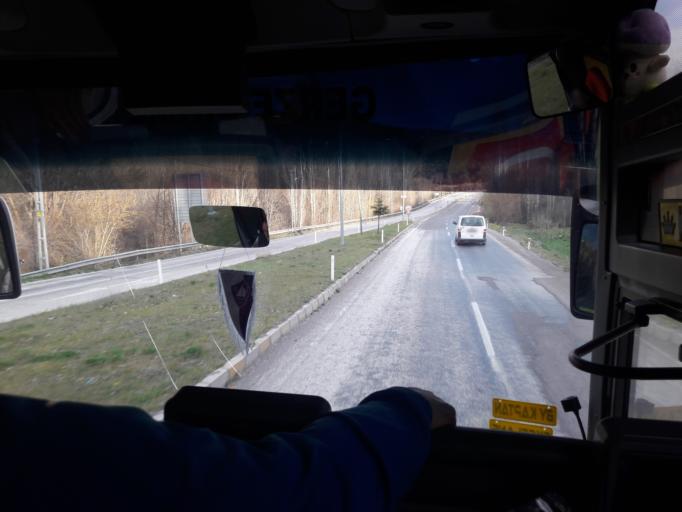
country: TR
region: Cankiri
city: Korgun
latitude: 40.7335
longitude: 33.5223
